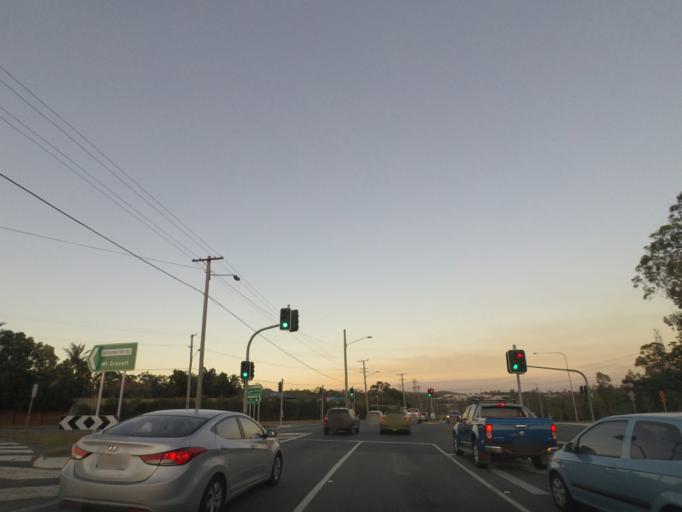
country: AU
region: Queensland
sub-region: Brisbane
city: Mackenzie
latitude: -27.5468
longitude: 153.1108
